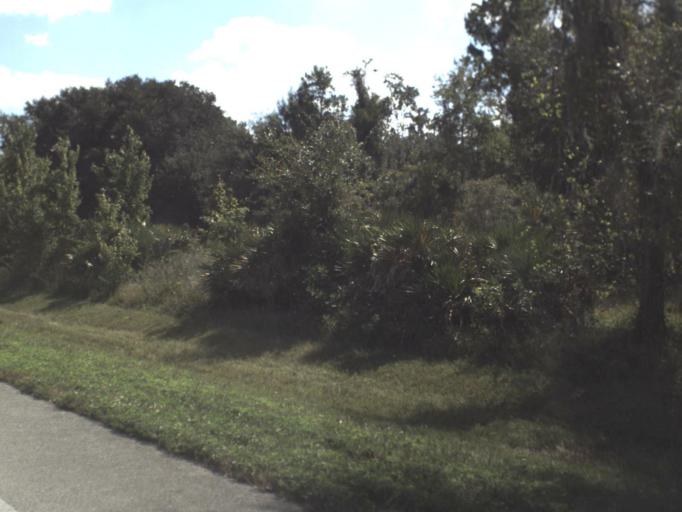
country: US
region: Florida
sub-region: Hardee County
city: Zolfo Springs
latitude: 27.4496
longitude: -81.6316
